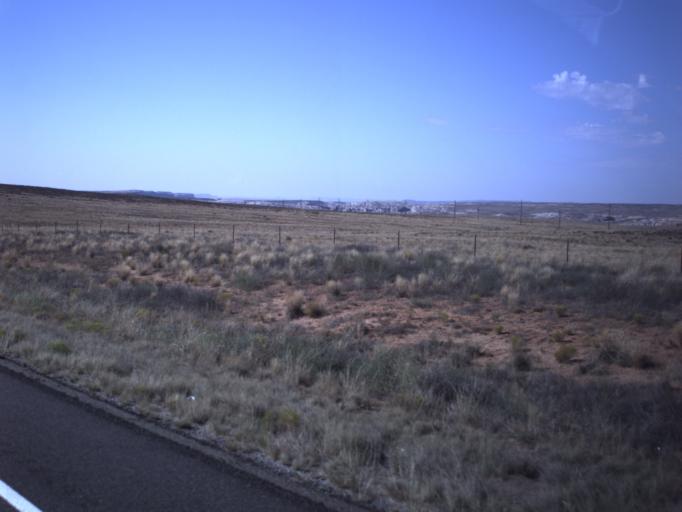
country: US
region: Utah
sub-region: San Juan County
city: Blanding
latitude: 37.3421
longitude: -109.5197
